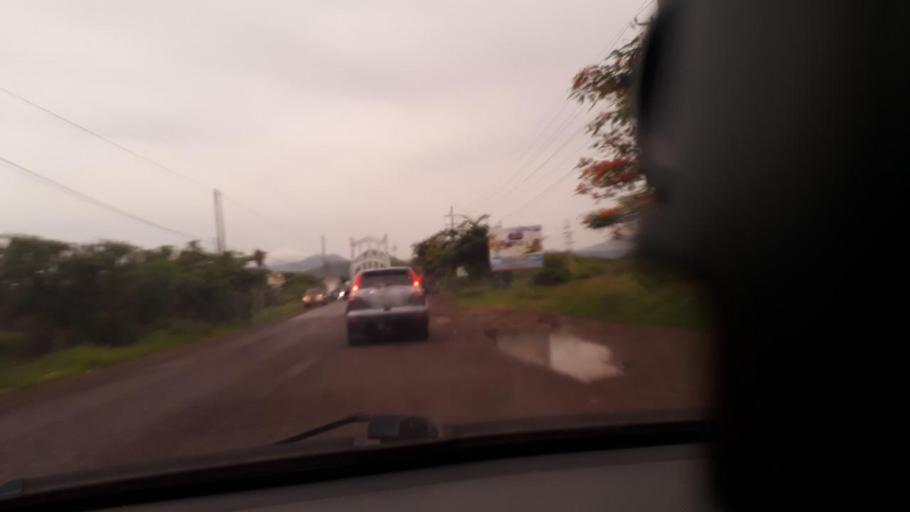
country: GT
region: Jutiapa
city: Asuncion Mita
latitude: 14.3059
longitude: -89.7171
